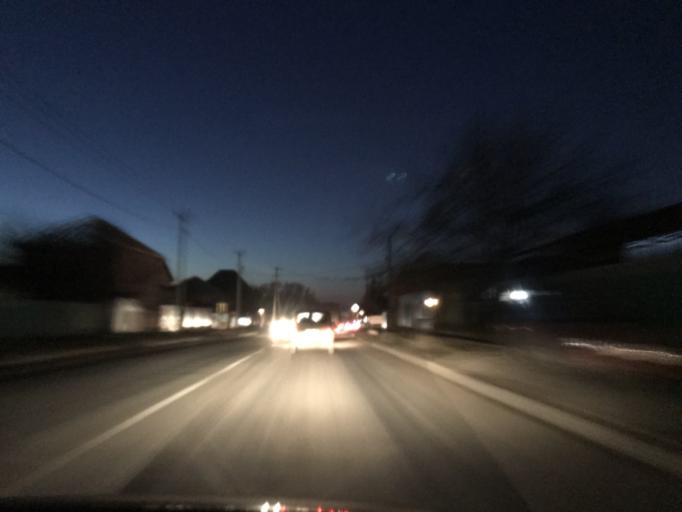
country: RU
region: Rostov
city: Rostov-na-Donu
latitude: 47.1929
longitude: 39.6183
